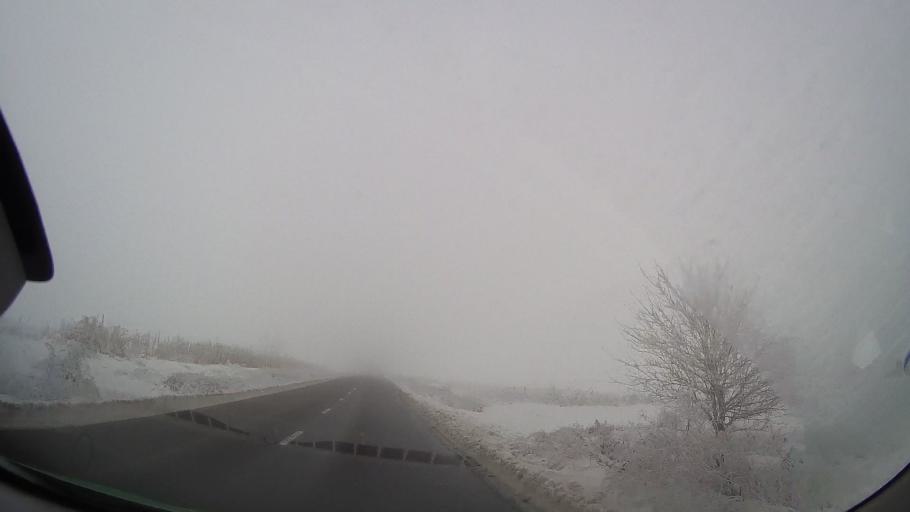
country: RO
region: Neamt
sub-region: Comuna Sabaoani
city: Sabaoani
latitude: 47.0348
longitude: 26.8551
